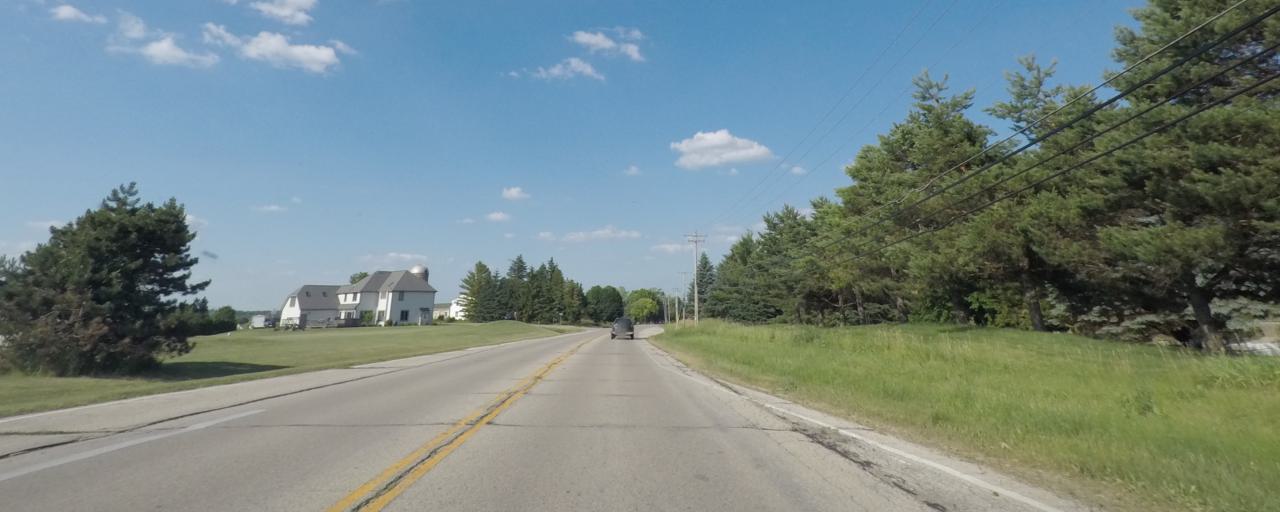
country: US
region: Wisconsin
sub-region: Waukesha County
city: Big Bend
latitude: 42.8684
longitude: -88.2238
